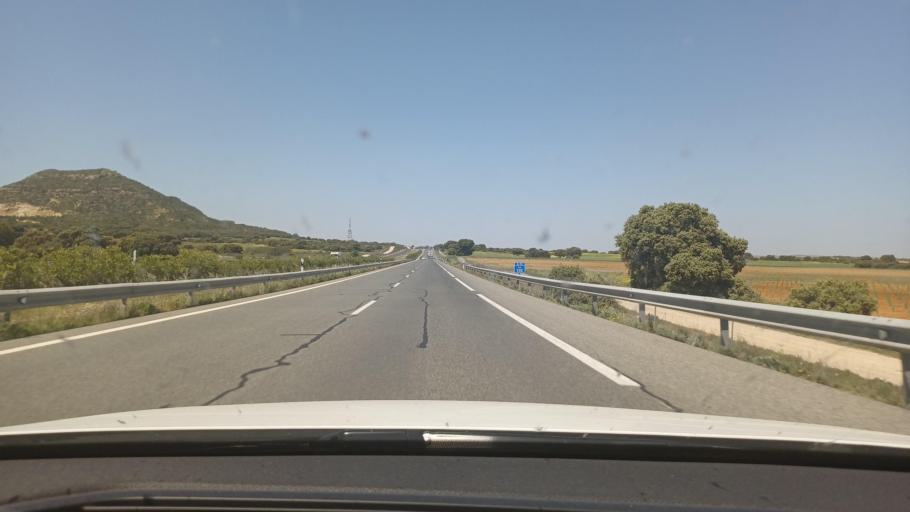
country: ES
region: Castille-La Mancha
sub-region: Provincia de Albacete
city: Corral-Rubio
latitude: 38.8990
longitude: -1.4559
